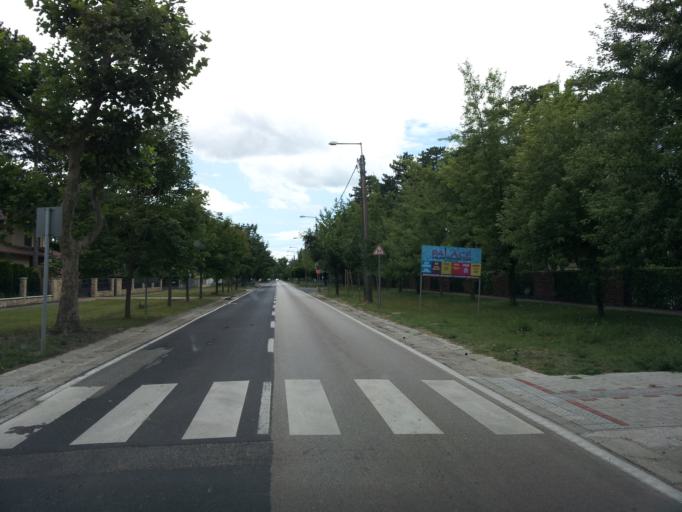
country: HU
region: Somogy
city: Siofok
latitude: 46.9028
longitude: 18.0302
